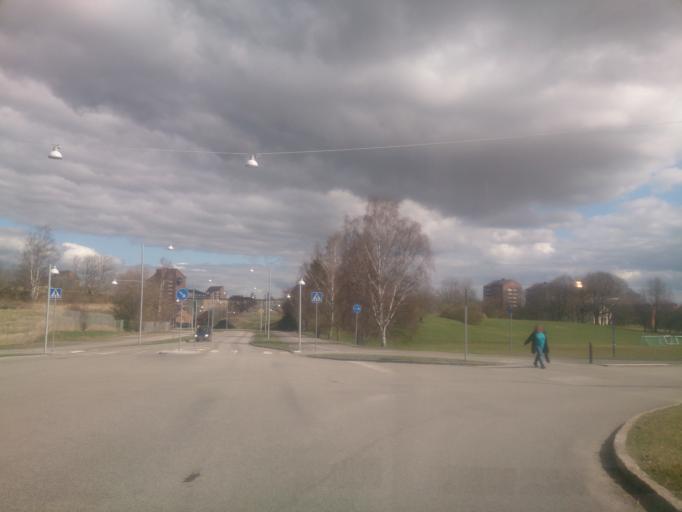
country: SE
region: OEstergoetland
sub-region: Norrkopings Kommun
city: Norrkoping
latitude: 58.5813
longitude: 16.1723
